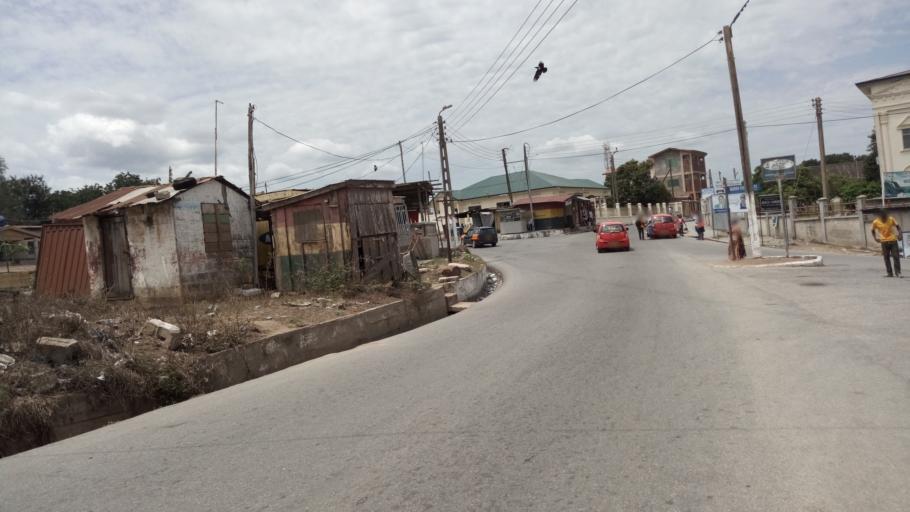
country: GH
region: Central
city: Winneba
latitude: 5.3421
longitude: -0.6240
